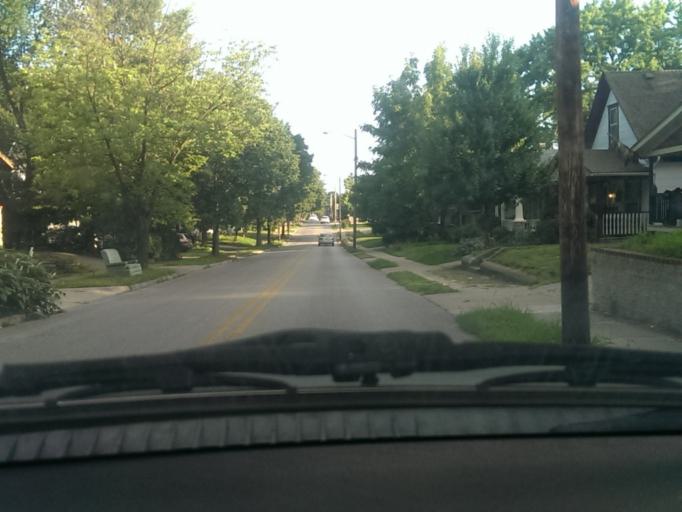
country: US
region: Kansas
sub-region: Johnson County
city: Westwood
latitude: 39.0482
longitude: -94.6074
